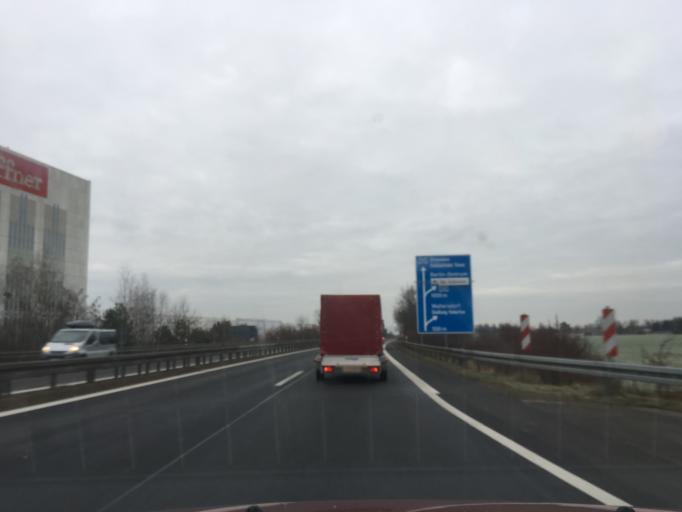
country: DE
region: Berlin
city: Bohnsdorf
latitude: 52.3744
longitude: 13.5604
